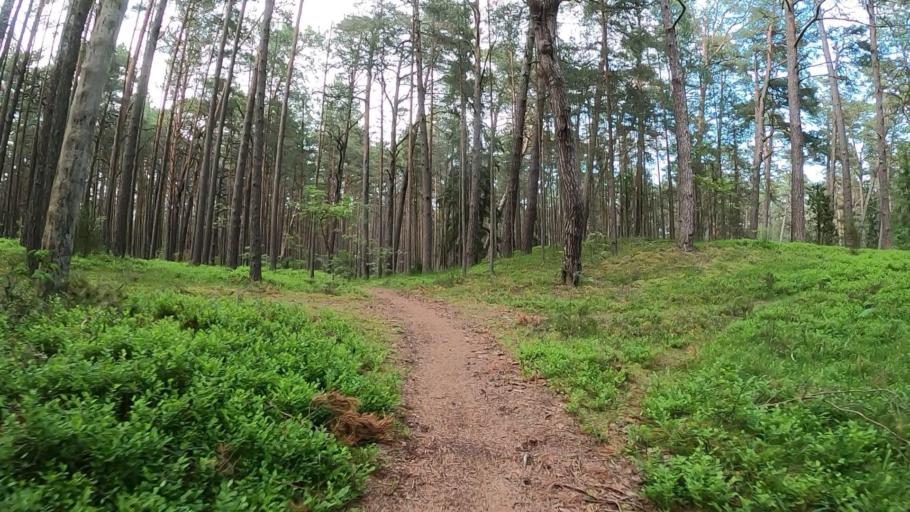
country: LV
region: Carnikava
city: Carnikava
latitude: 57.1197
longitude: 24.2067
